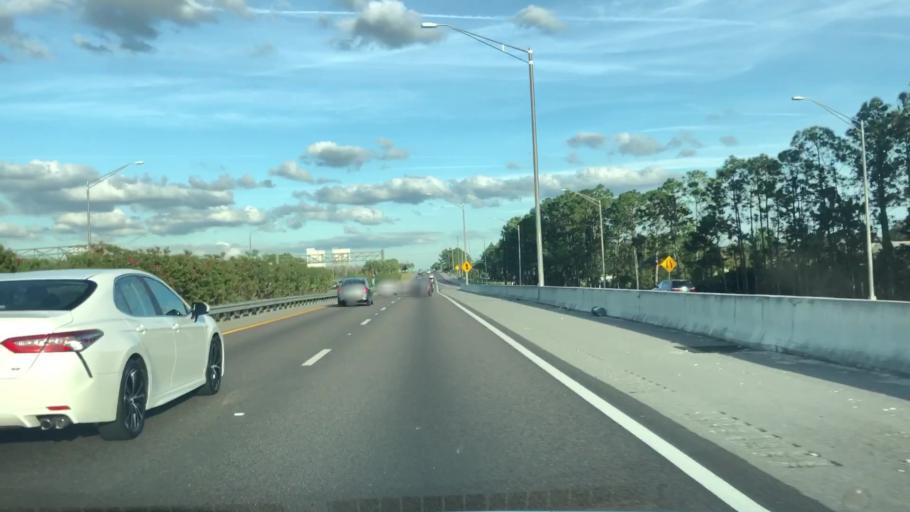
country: US
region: Florida
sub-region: Orange County
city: Hunters Creek
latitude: 28.3557
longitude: -81.4585
